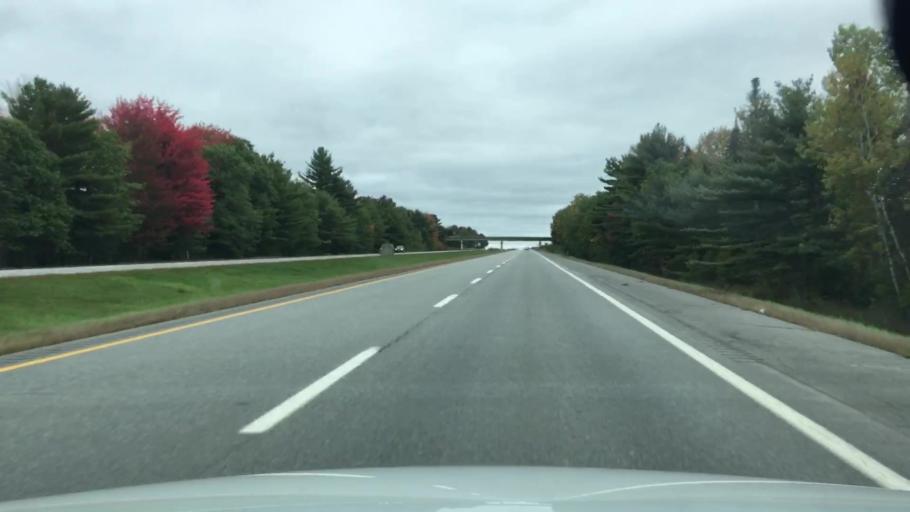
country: US
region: Maine
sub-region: Penobscot County
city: Newport
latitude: 44.8210
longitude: -69.2649
